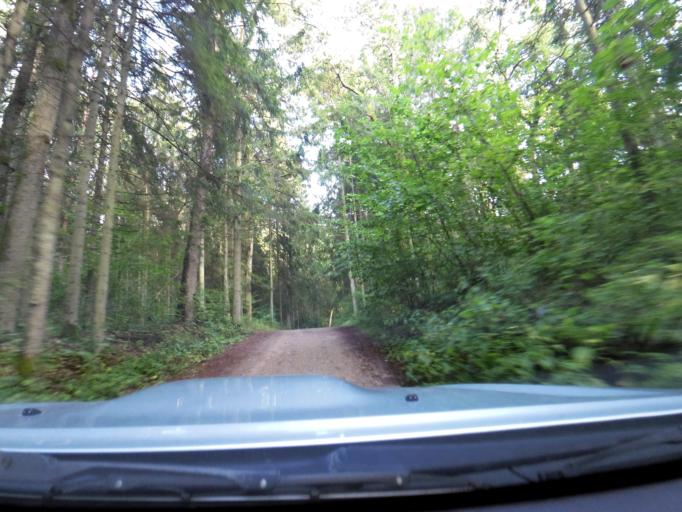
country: LT
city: Trakai
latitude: 54.6476
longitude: 24.9671
